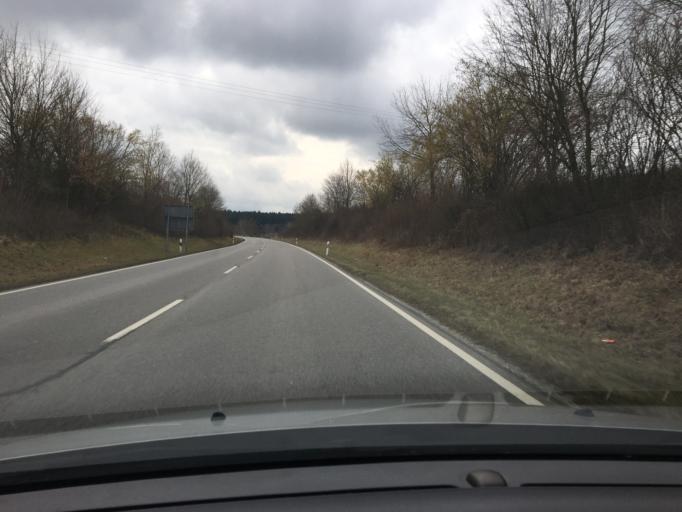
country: DE
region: Bavaria
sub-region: Lower Bavaria
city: Schalkham
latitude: 48.4443
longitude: 12.4262
